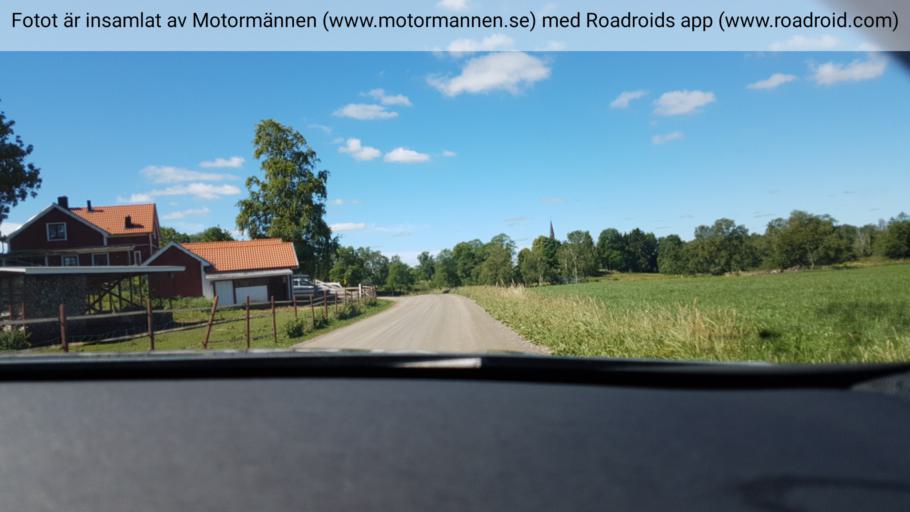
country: SE
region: Vaestra Goetaland
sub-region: Falkopings Kommun
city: Akarp
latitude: 58.1959
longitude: 13.7269
